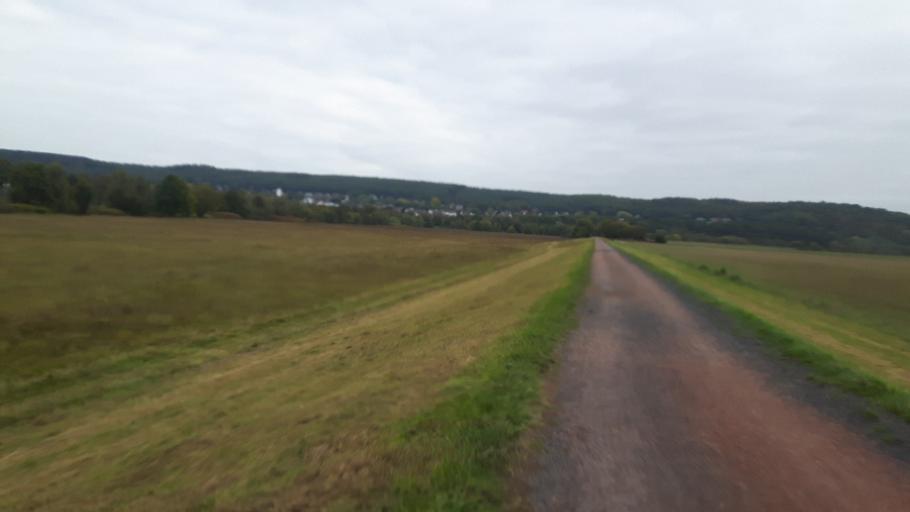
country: DE
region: North Rhine-Westphalia
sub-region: Regierungsbezirk Koln
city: Stossdorf
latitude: 50.7924
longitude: 7.2502
